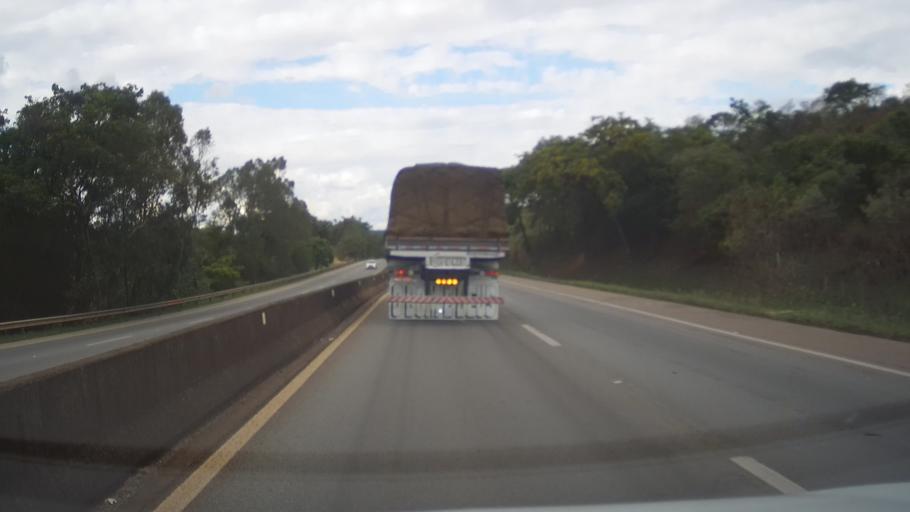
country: BR
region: Minas Gerais
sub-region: Itauna
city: Itauna
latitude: -20.3150
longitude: -44.4526
